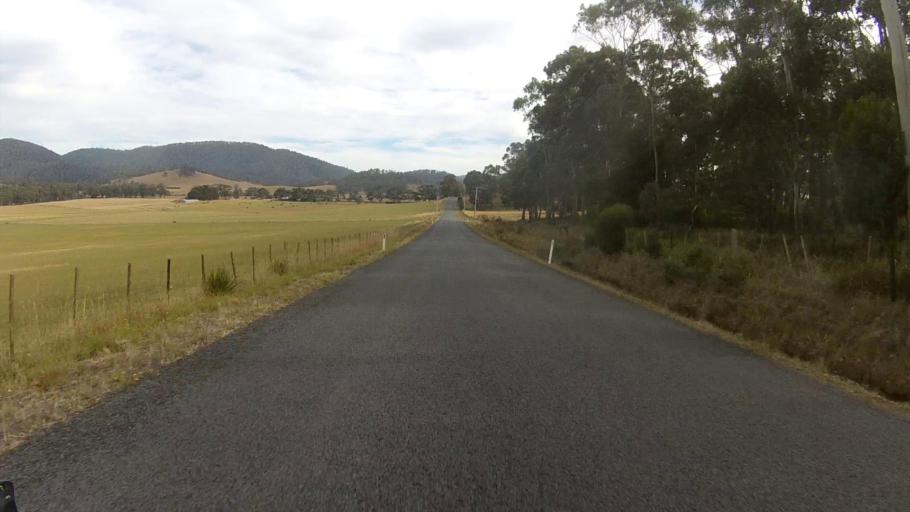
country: AU
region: Tasmania
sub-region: Sorell
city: Sorell
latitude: -42.8003
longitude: 147.7936
